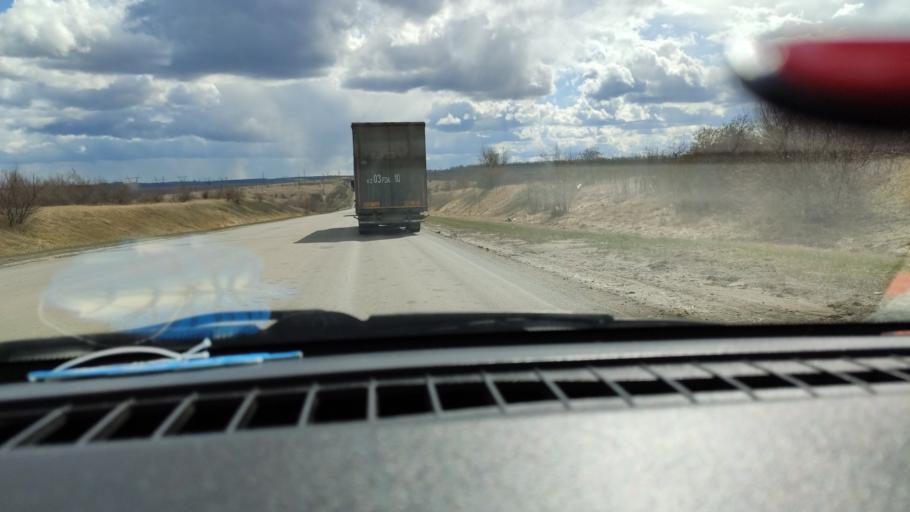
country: RU
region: Samara
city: Varlamovo
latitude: 53.0983
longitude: 48.3563
